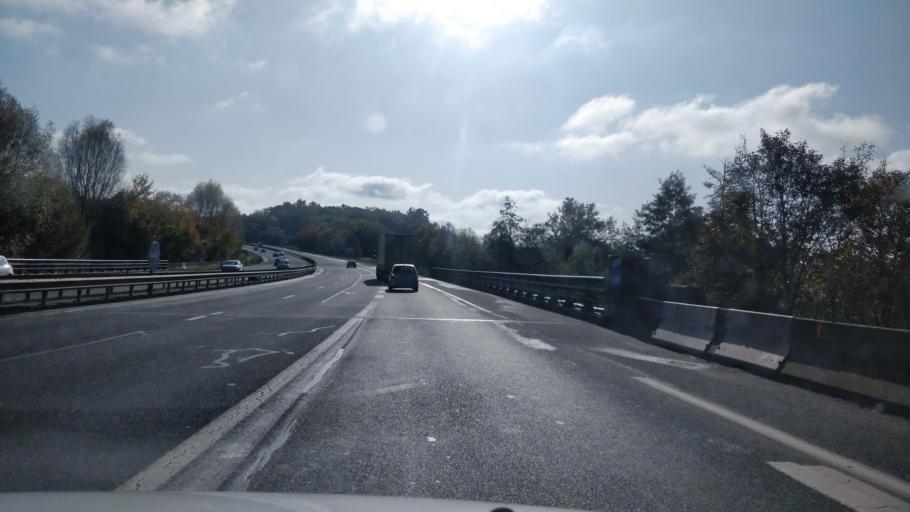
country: FR
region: Lower Normandy
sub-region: Departement du Calvados
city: Bretteville-sur-Odon
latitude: 49.1607
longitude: -0.4274
